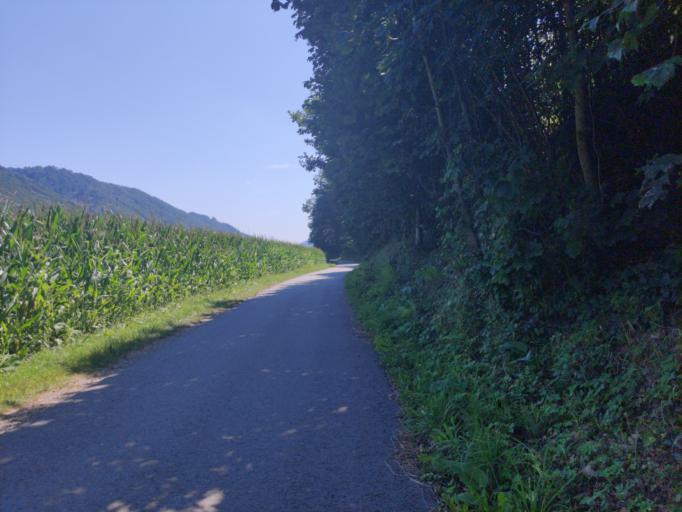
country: AT
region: Upper Austria
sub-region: Politischer Bezirk Rohrbach
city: Pfarrkirchen im Muehlkreis
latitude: 48.4950
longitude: 13.7366
